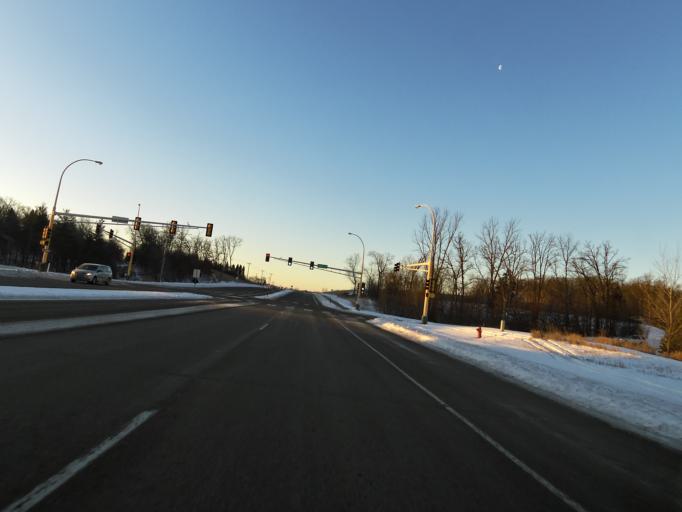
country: US
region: Minnesota
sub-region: Scott County
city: Prior Lake
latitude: 44.7257
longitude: -93.3736
